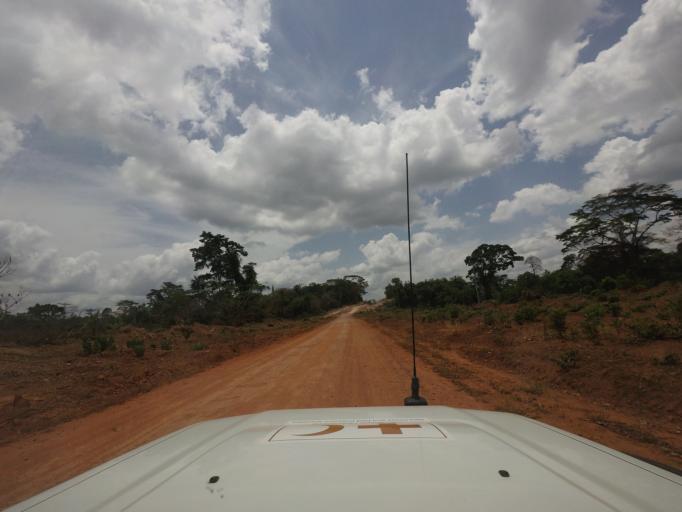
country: LR
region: Nimba
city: Sanniquellie
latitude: 7.2684
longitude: -8.8437
